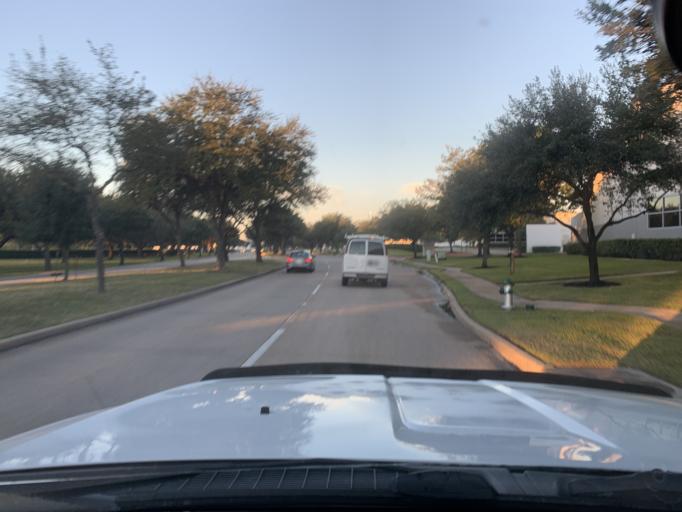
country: US
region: Texas
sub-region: Fort Bend County
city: Meadows Place
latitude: 29.6472
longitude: -95.6029
